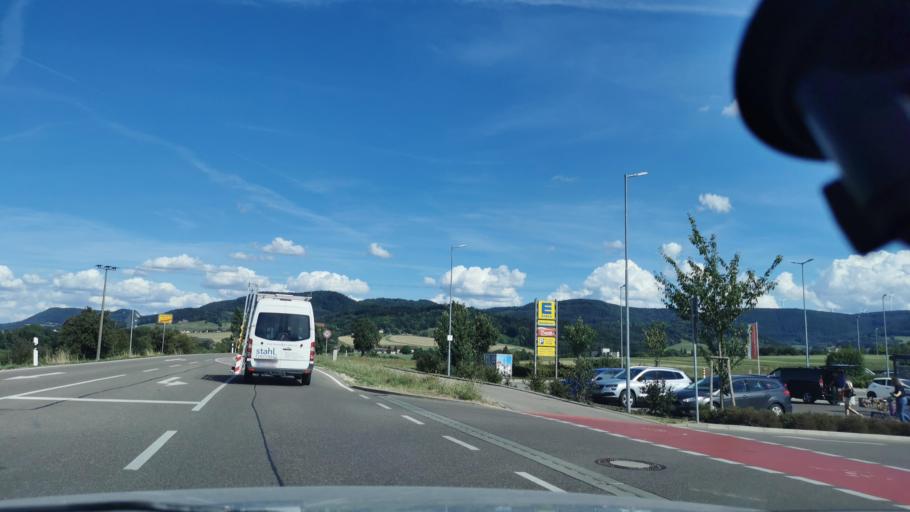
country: DE
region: Baden-Wuerttemberg
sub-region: Regierungsbezirk Stuttgart
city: Waldstetten
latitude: 48.7833
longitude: 9.8541
